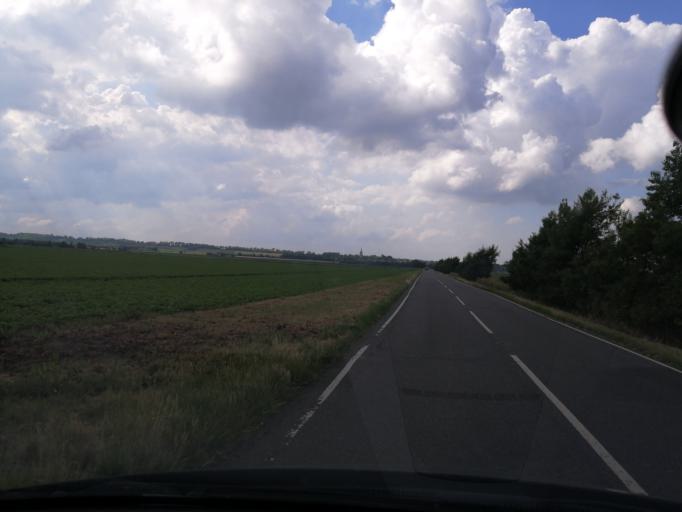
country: GB
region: England
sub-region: Cambridgeshire
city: Yaxley
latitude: 52.4986
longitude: -0.2482
